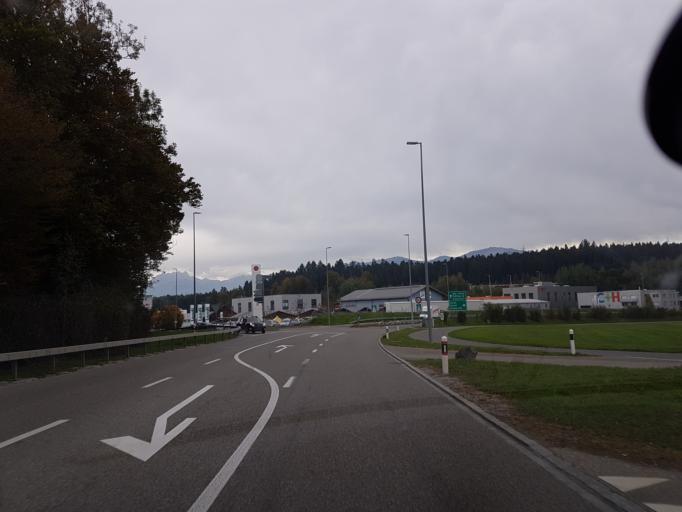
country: CH
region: Saint Gallen
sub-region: Wahlkreis See-Gaster
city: Schmerikon
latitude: 47.2395
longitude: 8.9502
